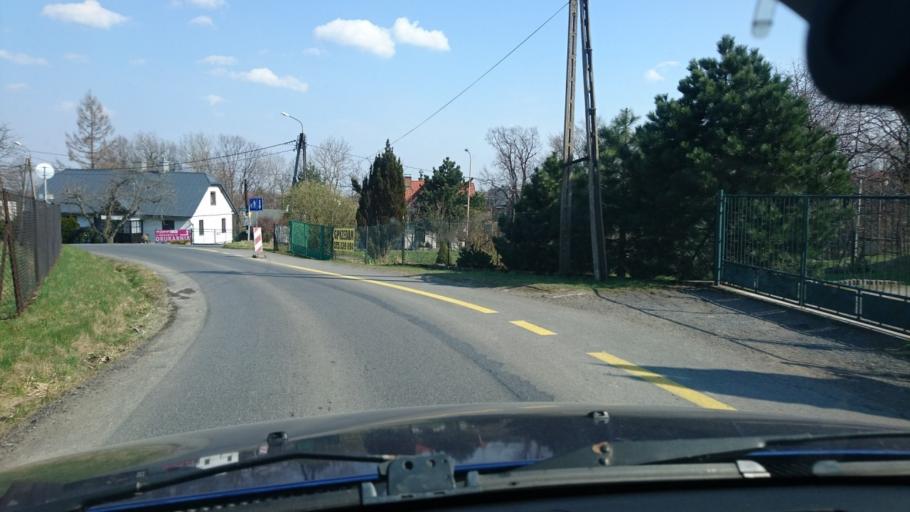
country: PL
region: Silesian Voivodeship
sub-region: Powiat bielski
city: Kozy
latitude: 49.8212
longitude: 19.1167
